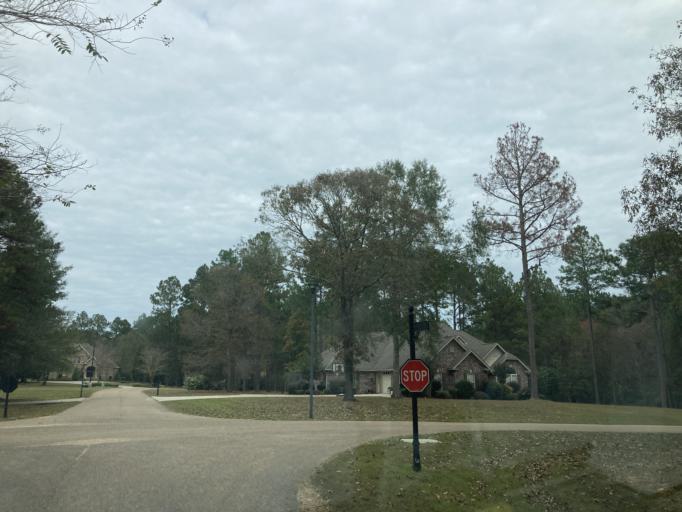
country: US
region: Mississippi
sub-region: Lamar County
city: West Hattiesburg
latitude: 31.3019
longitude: -89.4476
